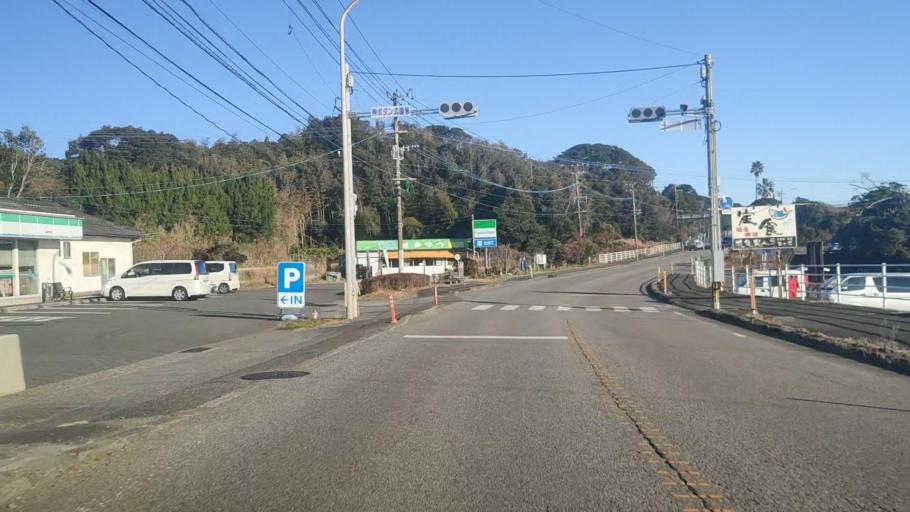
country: JP
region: Miyazaki
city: Nobeoka
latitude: 32.3565
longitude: 131.6211
